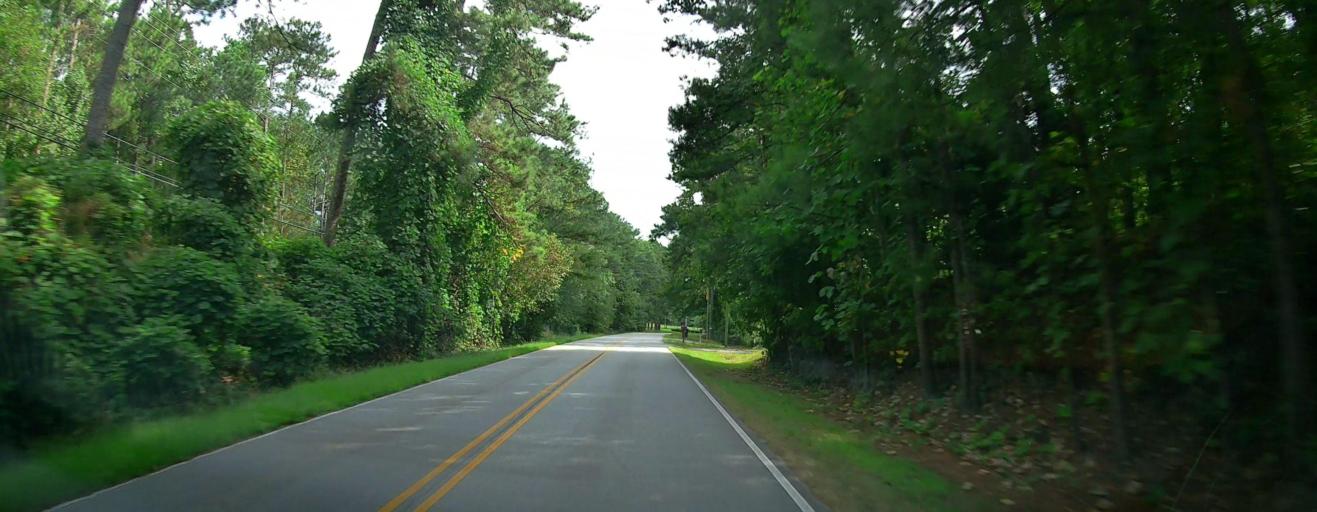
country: US
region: Alabama
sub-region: Russell County
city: Phenix City
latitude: 32.5988
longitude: -84.9796
